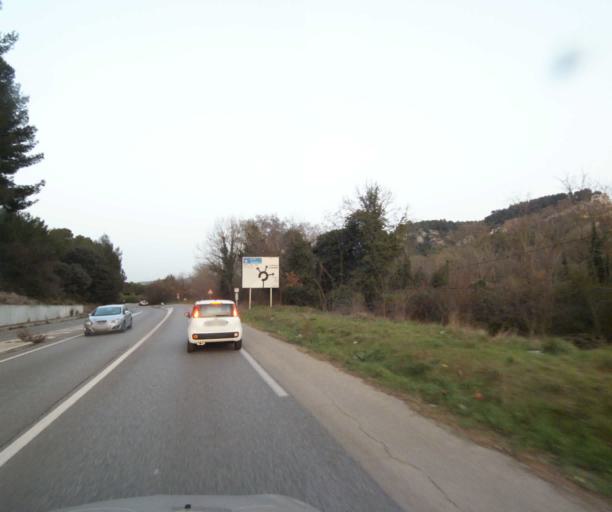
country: FR
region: Provence-Alpes-Cote d'Azur
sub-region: Departement des Bouches-du-Rhone
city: Cabries
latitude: 43.4267
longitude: 5.4001
